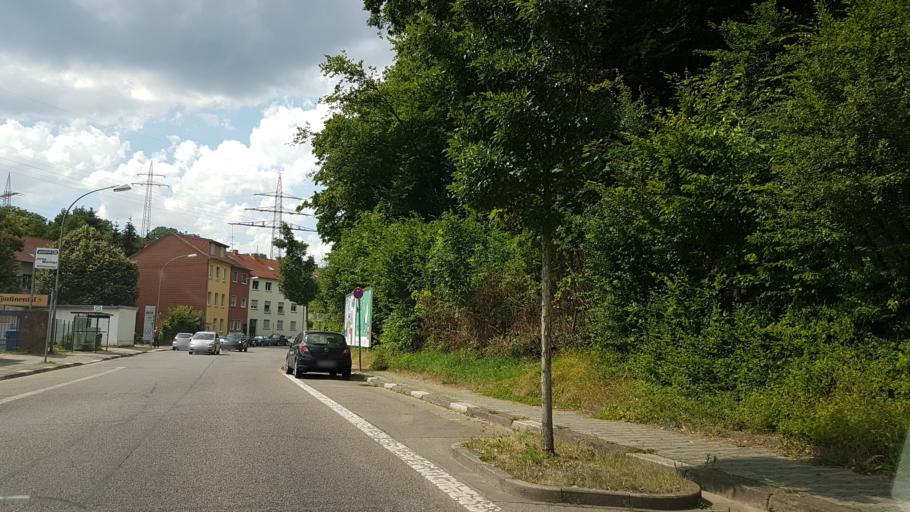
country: DE
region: Saarland
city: Saarbrucken
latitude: 49.2523
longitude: 6.9771
